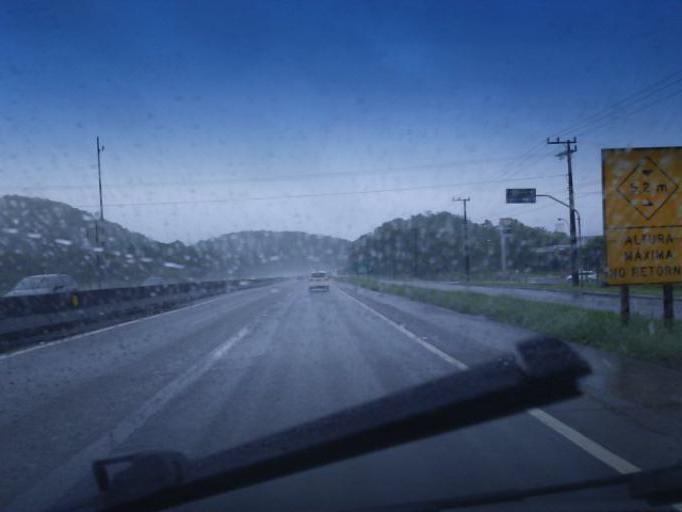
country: BR
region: Santa Catarina
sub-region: Joinville
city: Joinville
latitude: -26.3062
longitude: -48.8804
